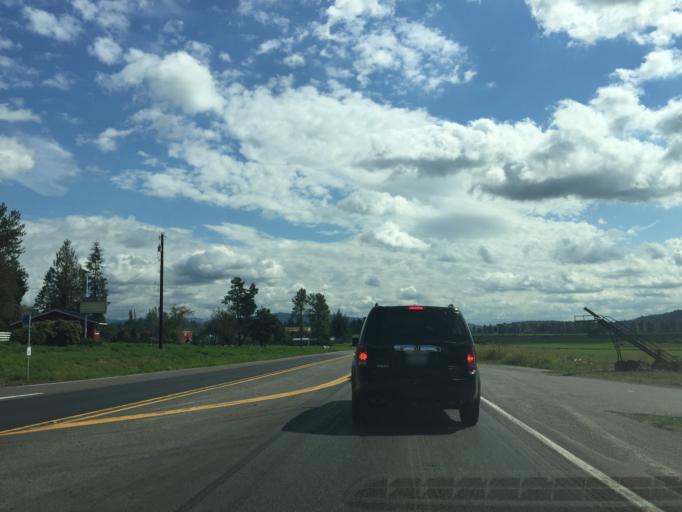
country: US
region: Washington
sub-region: Snohomish County
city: Three Lakes
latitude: 47.9006
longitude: -122.0366
